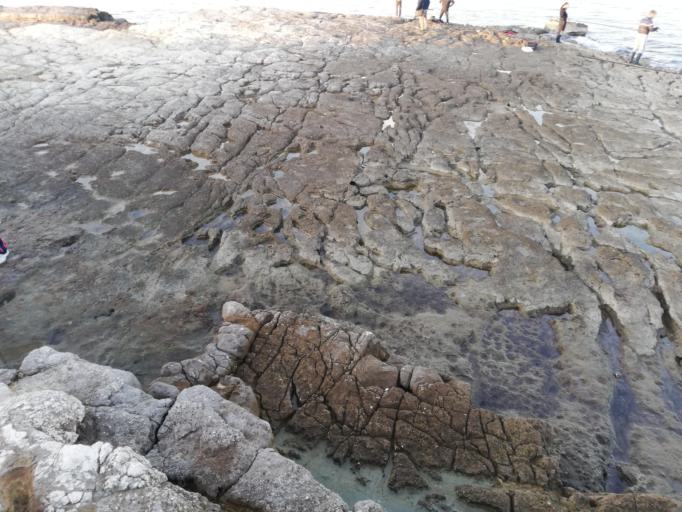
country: IT
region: Apulia
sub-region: Provincia di Bari
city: Molfetta
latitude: 41.2008
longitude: 16.6024
